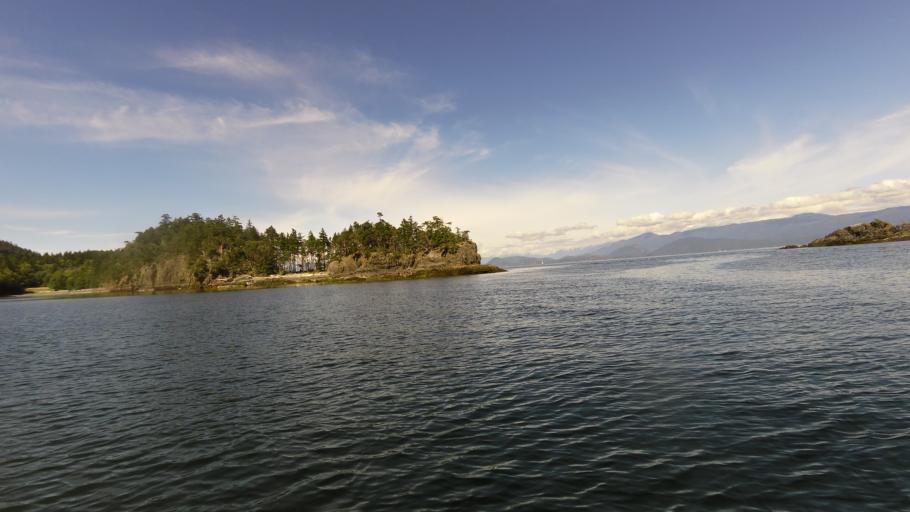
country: CA
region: British Columbia
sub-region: Regional District of Nanaimo
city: Parksville
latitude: 49.5149
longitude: -124.1347
